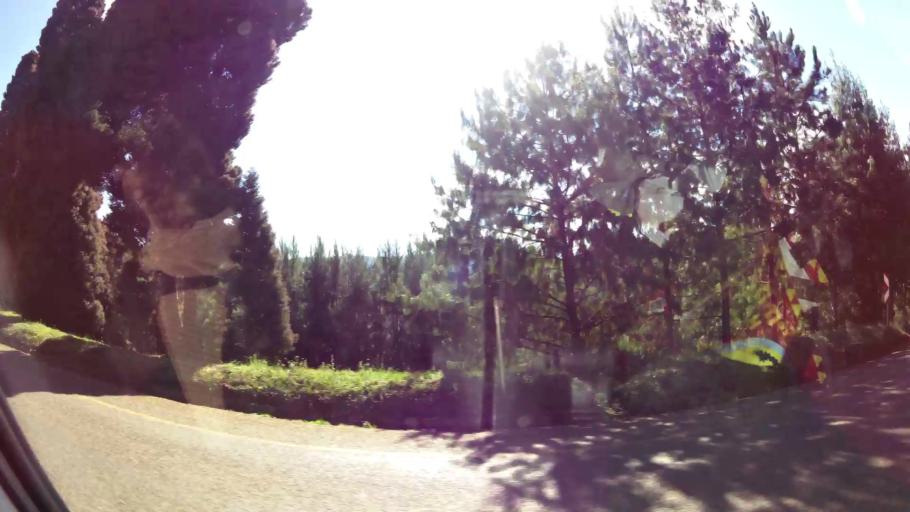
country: ZA
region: Limpopo
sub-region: Capricorn District Municipality
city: Mankoeng
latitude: -23.9069
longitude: 29.9859
